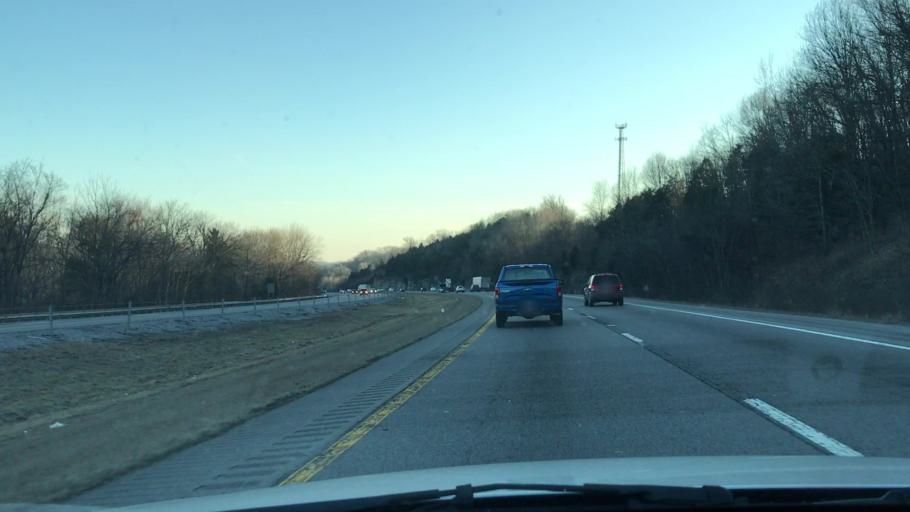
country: US
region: Tennessee
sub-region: Sumner County
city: Millersville
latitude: 36.3576
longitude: -86.7203
